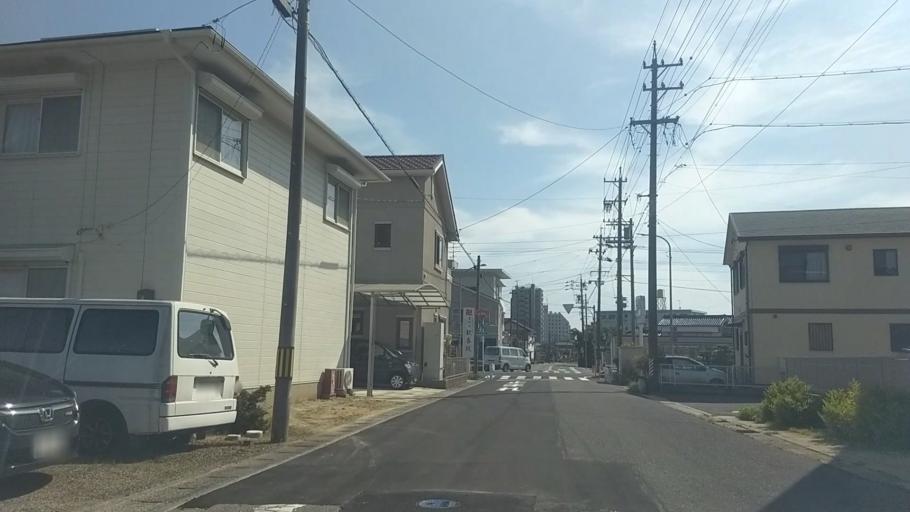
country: JP
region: Aichi
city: Anjo
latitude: 34.9638
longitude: 137.0922
